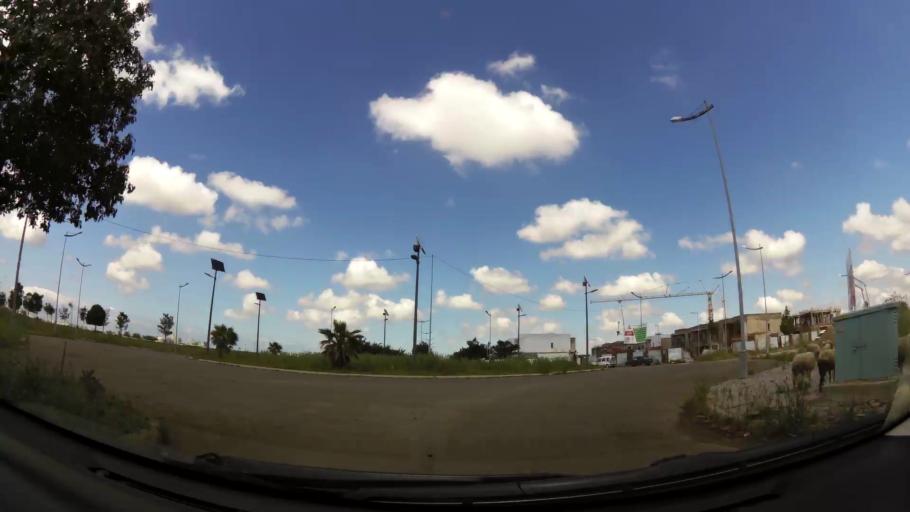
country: MA
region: Grand Casablanca
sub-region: Nouaceur
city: Dar Bouazza
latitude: 33.4179
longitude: -7.8275
